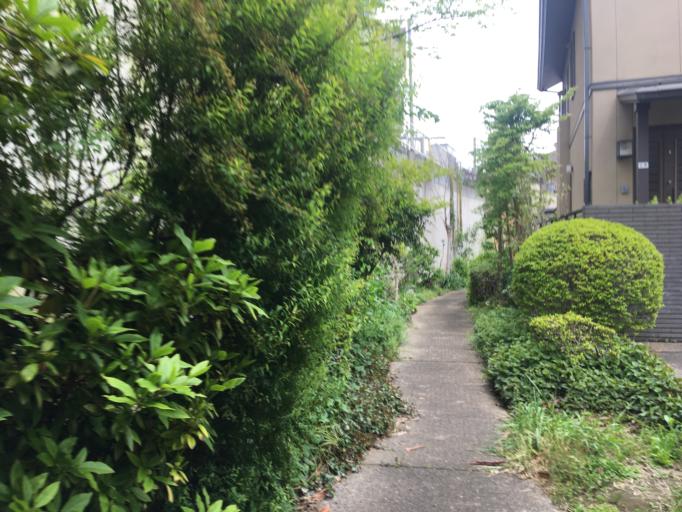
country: JP
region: Saitama
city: Oi
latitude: 35.8499
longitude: 139.5436
